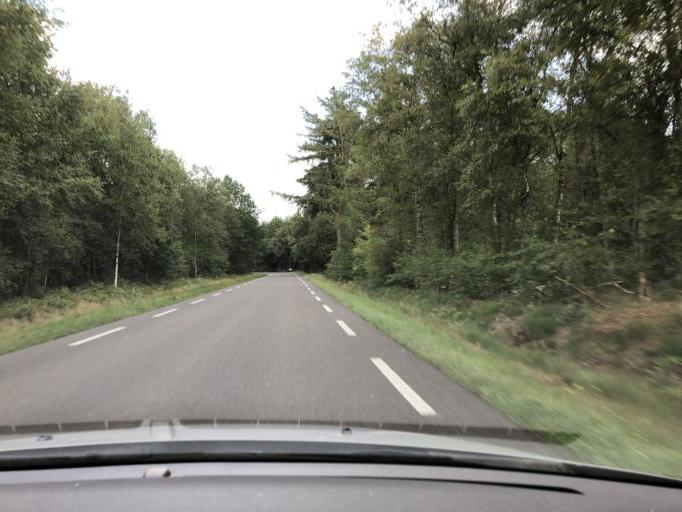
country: NL
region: Drenthe
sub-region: Gemeente Borger-Odoorn
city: Borger
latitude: 52.9399
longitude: 6.7292
